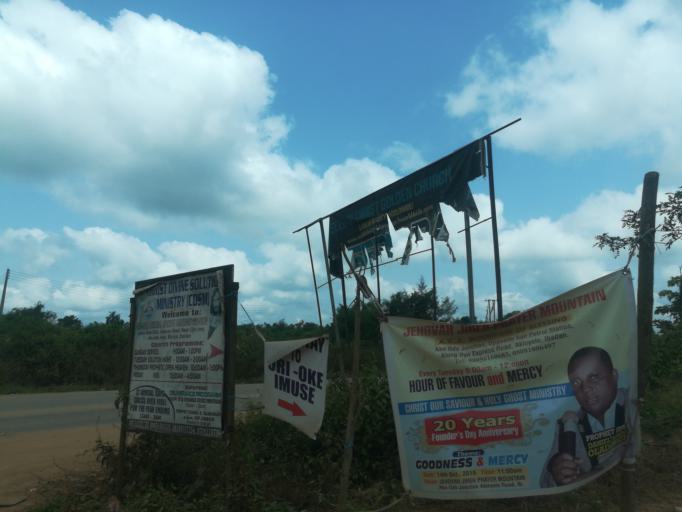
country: NG
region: Oyo
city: Moniya
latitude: 7.5718
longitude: 3.9148
